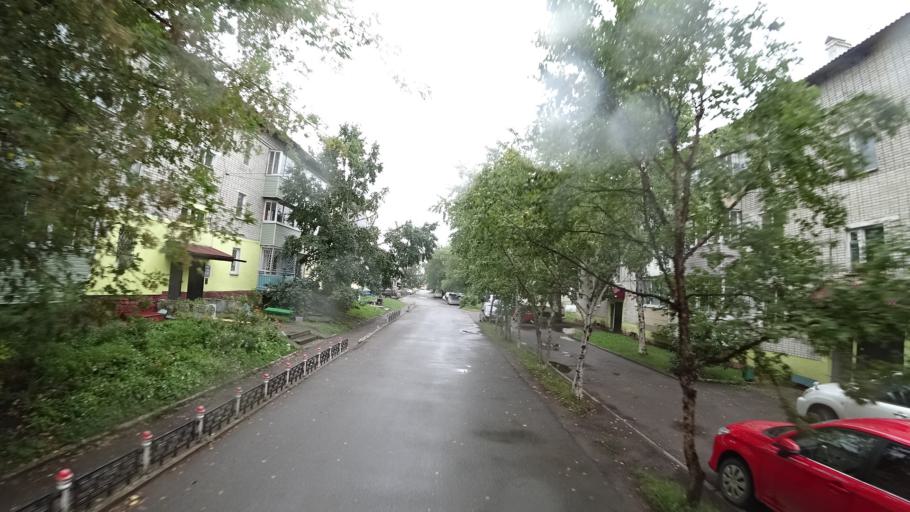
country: RU
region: Primorskiy
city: Monastyrishche
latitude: 44.1942
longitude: 132.4233
